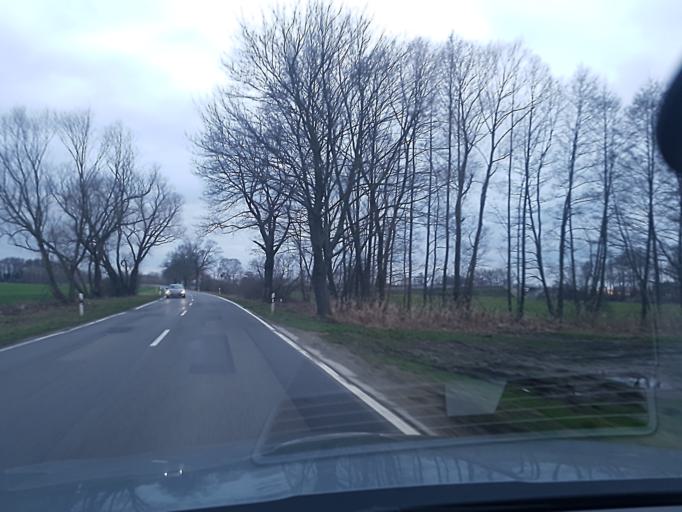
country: DE
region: Brandenburg
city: Schonewalde
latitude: 51.6706
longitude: 13.5902
